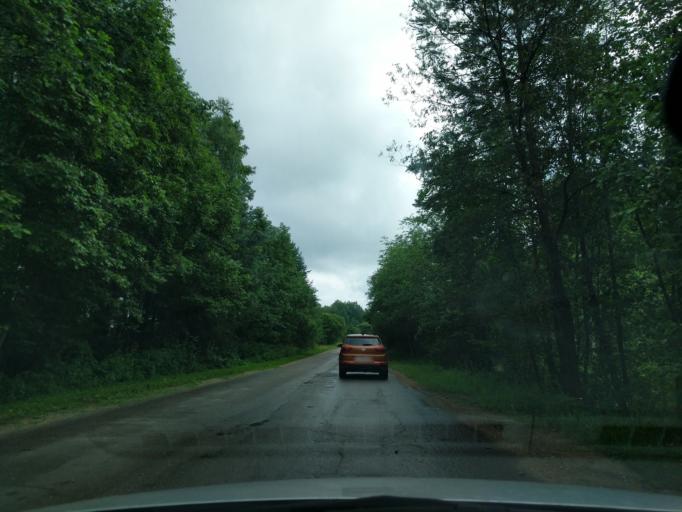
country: RU
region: Kaluga
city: Nikola-Lenivets
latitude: 54.7644
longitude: 35.7066
